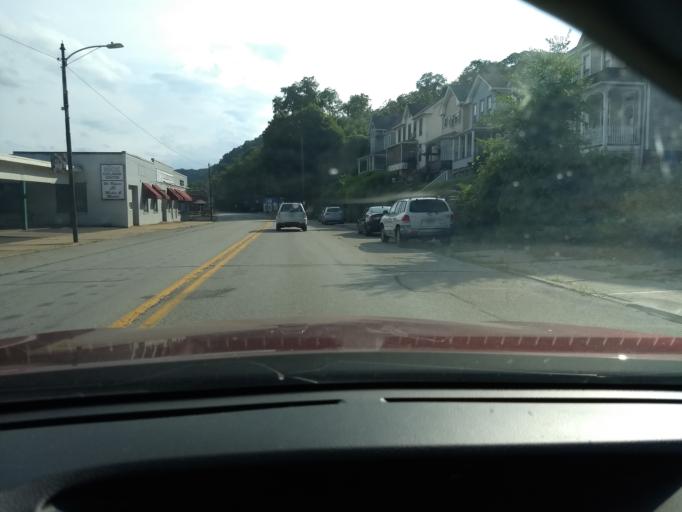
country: US
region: Pennsylvania
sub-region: Allegheny County
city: Tarentum
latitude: 40.5980
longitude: -79.7650
